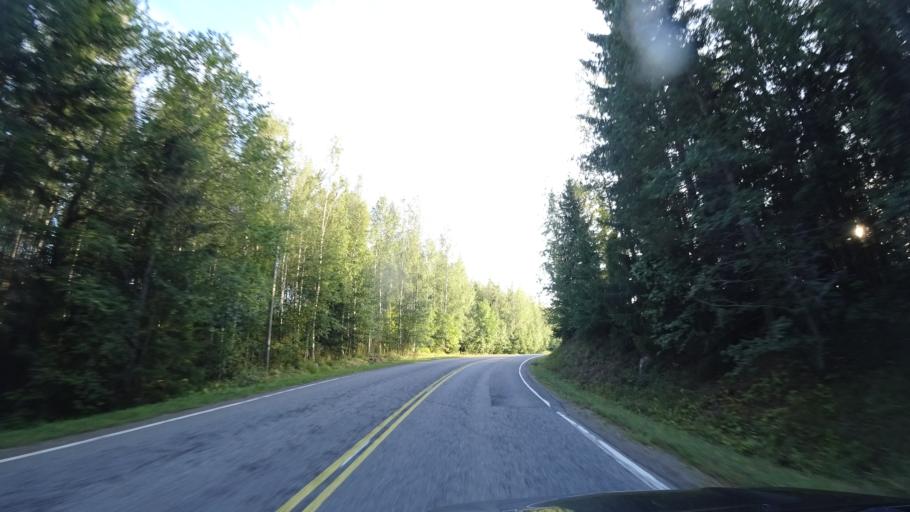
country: FI
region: Haeme
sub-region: Haemeenlinna
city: Lammi
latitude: 61.0383
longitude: 24.9334
